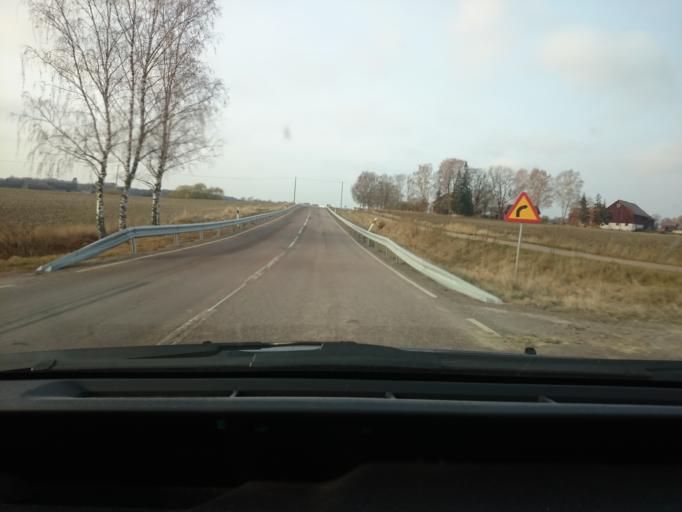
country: SE
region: Vaestmanland
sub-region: Vasteras
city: Skultuna
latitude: 59.6857
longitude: 16.4554
